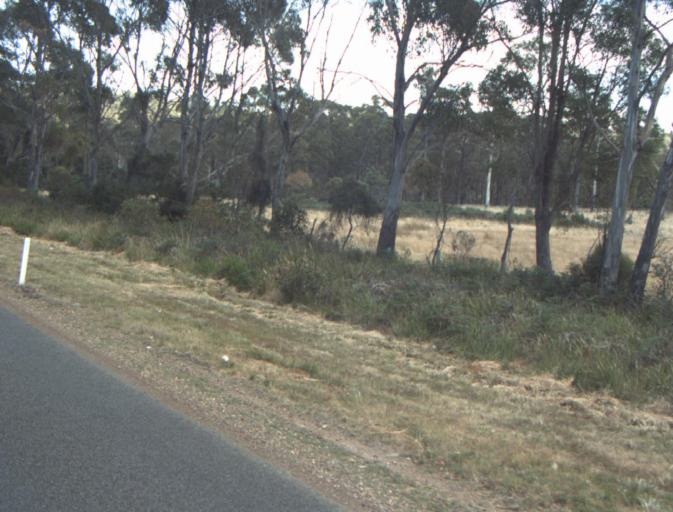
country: AU
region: Tasmania
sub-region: Launceston
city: Mayfield
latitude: -41.3175
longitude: 147.1351
